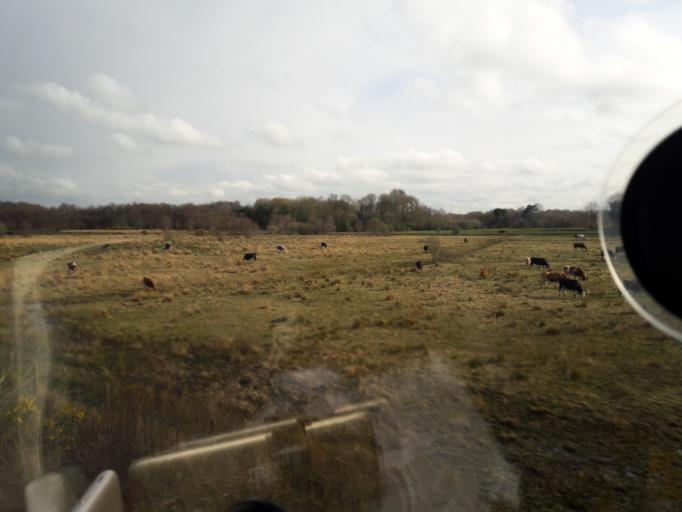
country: IE
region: Leinster
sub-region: An Iarmhi
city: Kinnegad
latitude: 53.4811
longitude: -7.0782
